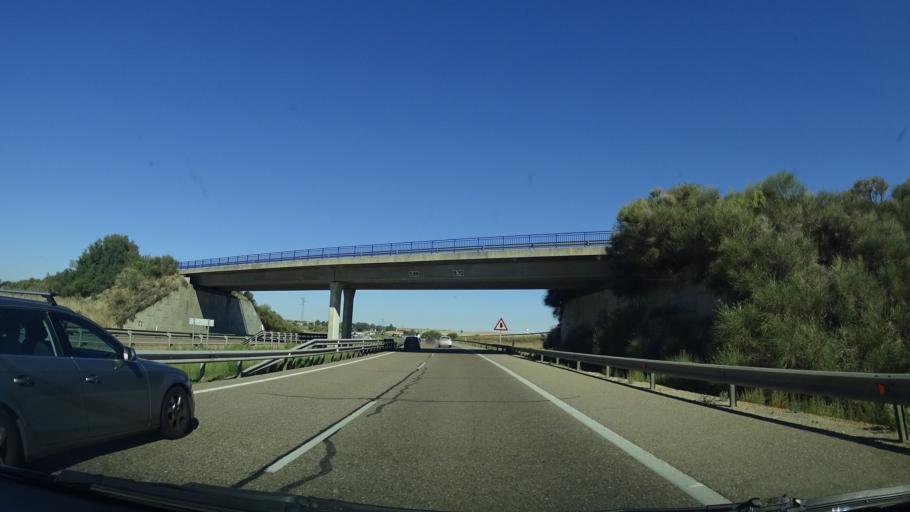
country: ES
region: Castille and Leon
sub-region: Provincia de Zamora
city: Cerecinos de Campos
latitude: 41.9020
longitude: -5.4773
